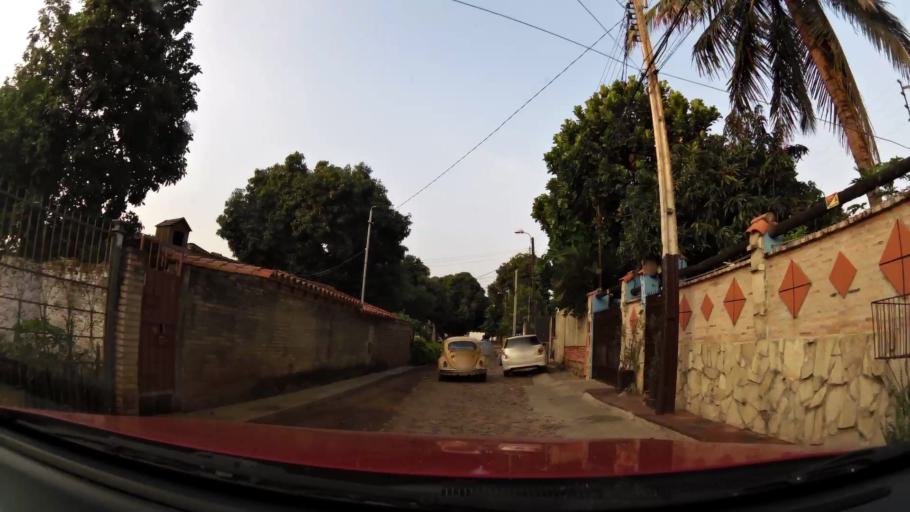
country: PY
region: Central
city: Lambare
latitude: -25.3535
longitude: -57.5975
